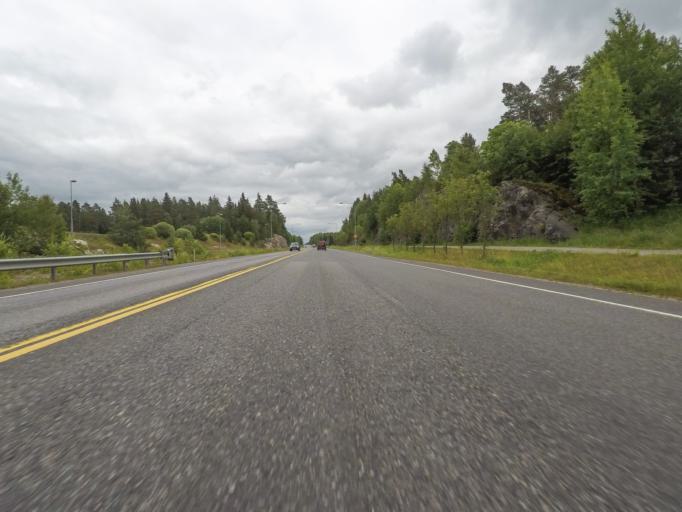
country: FI
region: Varsinais-Suomi
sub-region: Turku
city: Kaarina
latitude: 60.4700
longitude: 22.3679
